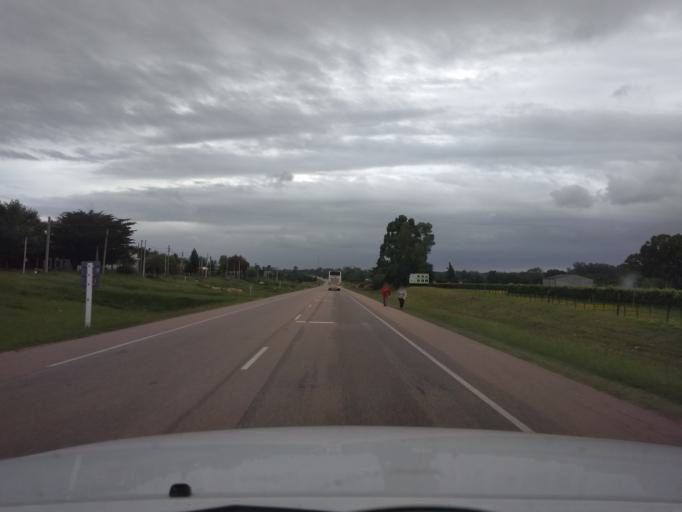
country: UY
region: Canelones
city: Canelones
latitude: -34.4924
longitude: -56.2819
